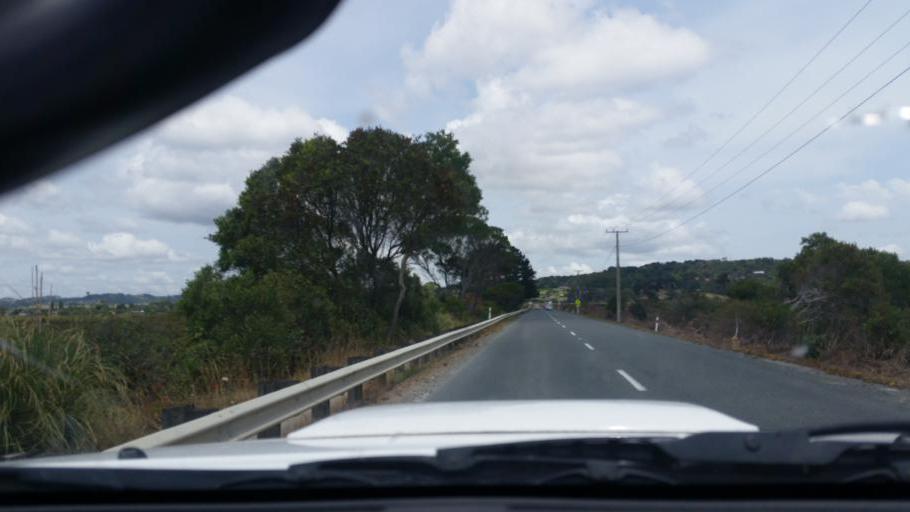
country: NZ
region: Auckland
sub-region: Auckland
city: Wellsford
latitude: -36.1090
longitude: 174.5790
